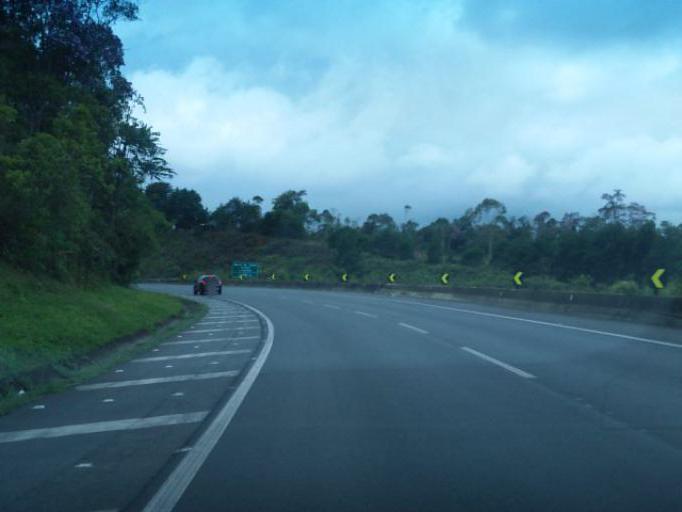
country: BR
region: Sao Paulo
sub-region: Cajati
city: Cajati
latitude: -24.9644
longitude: -48.4260
